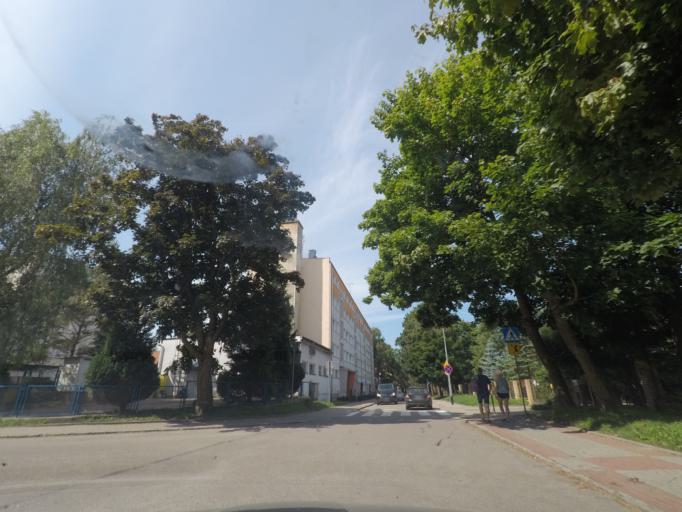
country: PL
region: West Pomeranian Voivodeship
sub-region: Powiat kolobrzeski
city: Kolobrzeg
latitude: 54.1925
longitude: 15.6642
